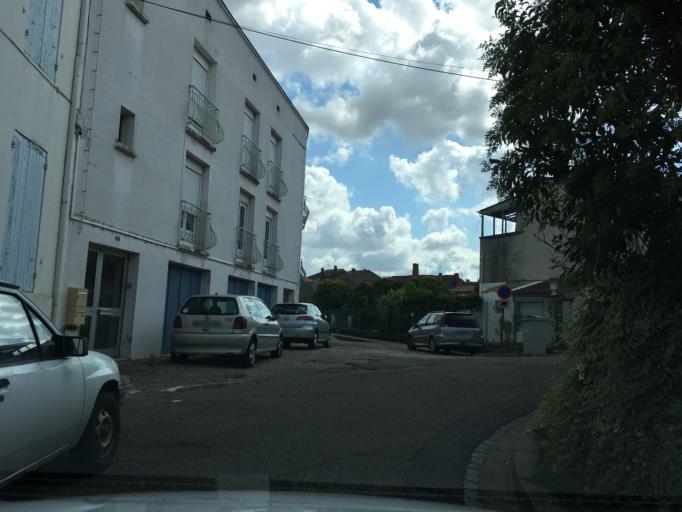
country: FR
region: Aquitaine
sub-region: Departement du Lot-et-Garonne
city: Agen
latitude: 44.2064
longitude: 0.6289
